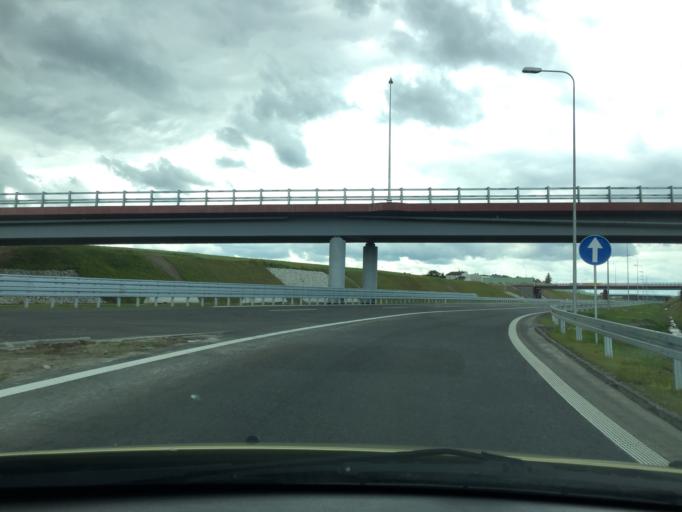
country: PL
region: Greater Poland Voivodeship
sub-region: Powiat jarocinski
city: Jarocin
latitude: 51.9779
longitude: 17.5250
